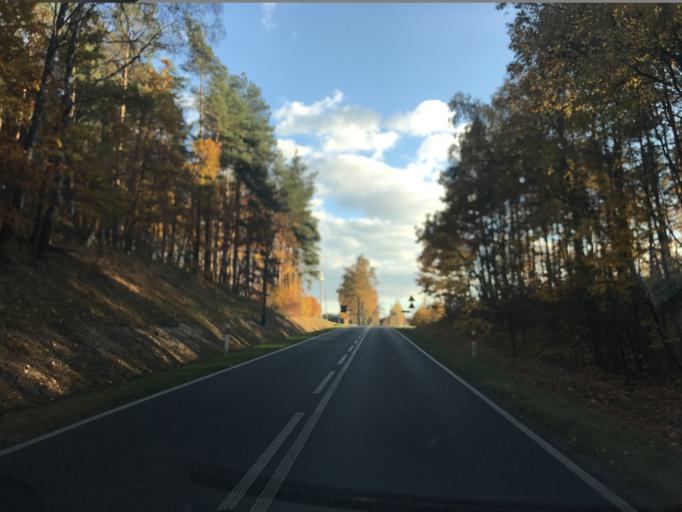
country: PL
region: Warmian-Masurian Voivodeship
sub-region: Powiat dzialdowski
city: Lidzbark
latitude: 53.2955
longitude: 19.8143
